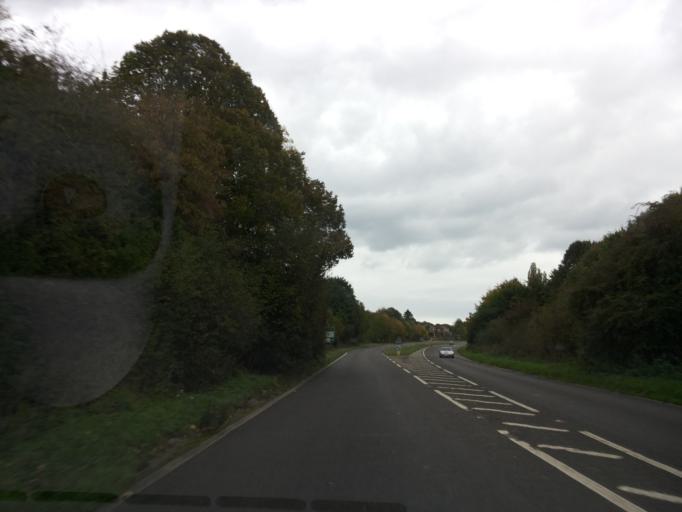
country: GB
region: England
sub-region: Buckinghamshire
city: Amersham
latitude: 51.6827
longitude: -0.6612
